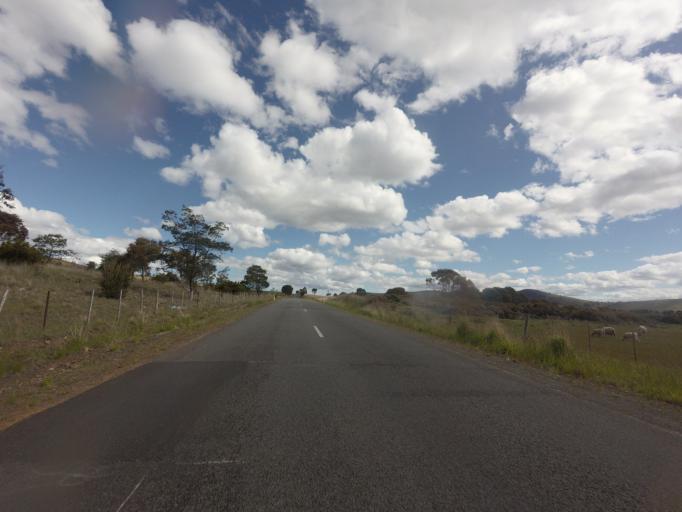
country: AU
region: Tasmania
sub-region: Brighton
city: Bridgewater
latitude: -42.3873
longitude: 147.3149
